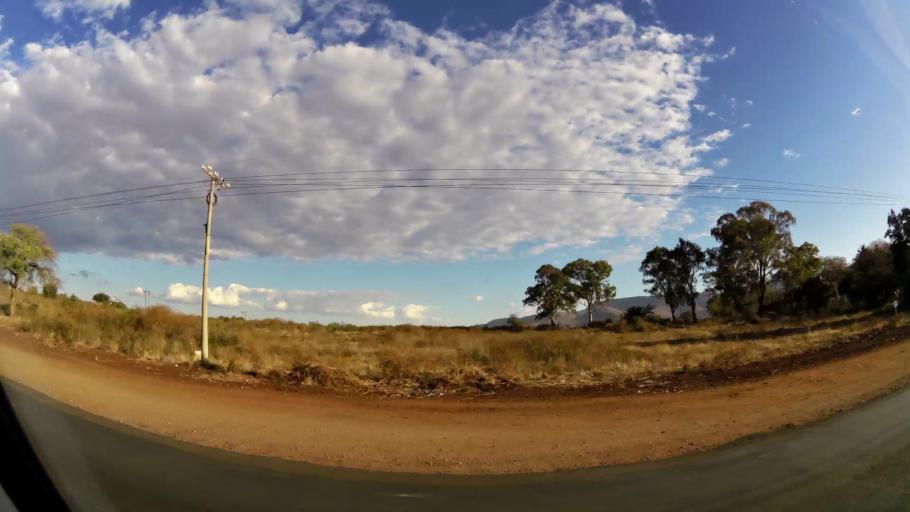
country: ZA
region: Limpopo
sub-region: Waterberg District Municipality
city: Mokopane
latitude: -24.1745
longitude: 28.9915
